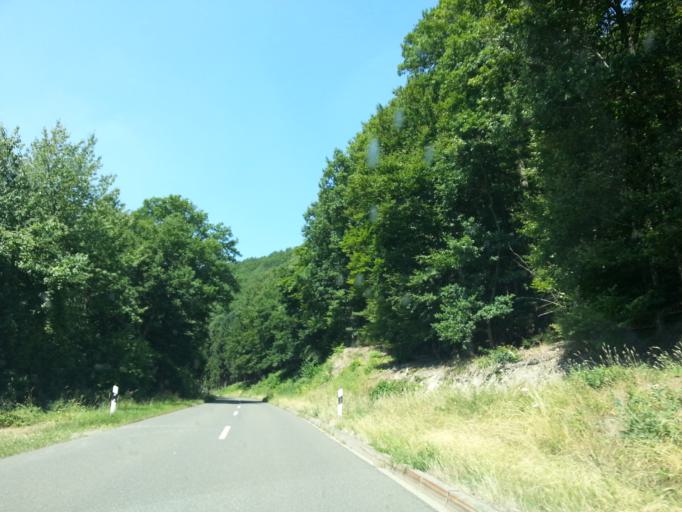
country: DE
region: Rheinland-Pfalz
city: Piesport
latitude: 49.8916
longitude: 6.9248
